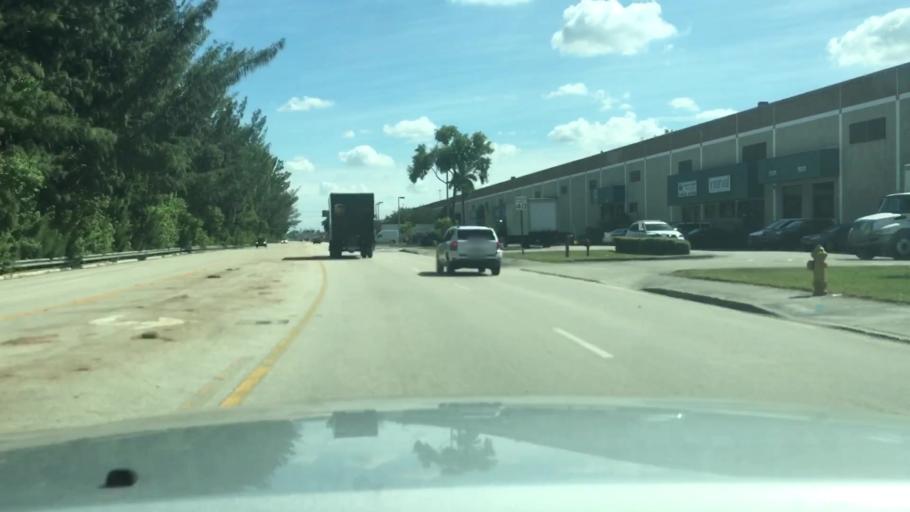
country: US
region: Florida
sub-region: Miami-Dade County
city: Fountainebleau
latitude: 25.7832
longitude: -80.3466
